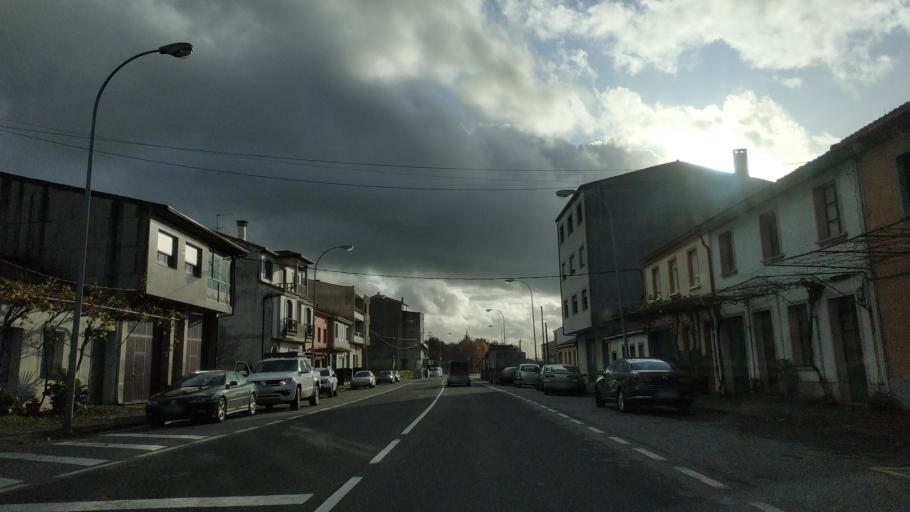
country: ES
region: Galicia
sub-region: Provincia da Coruna
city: Arzua
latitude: 42.9359
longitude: -8.1611
